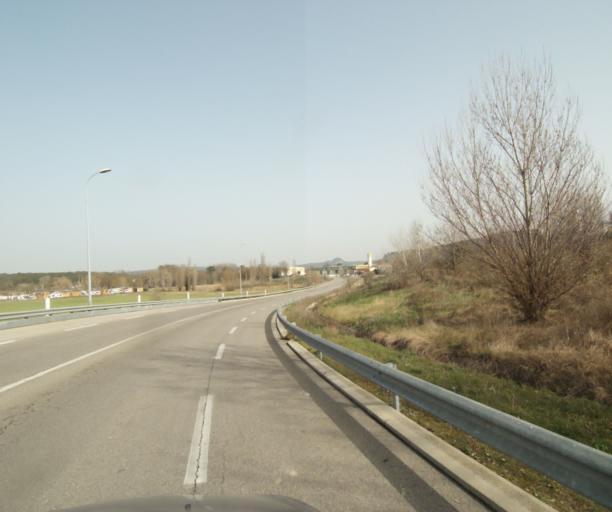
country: FR
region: Provence-Alpes-Cote d'Azur
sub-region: Departement des Bouches-du-Rhone
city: Cabries
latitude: 43.4217
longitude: 5.3804
